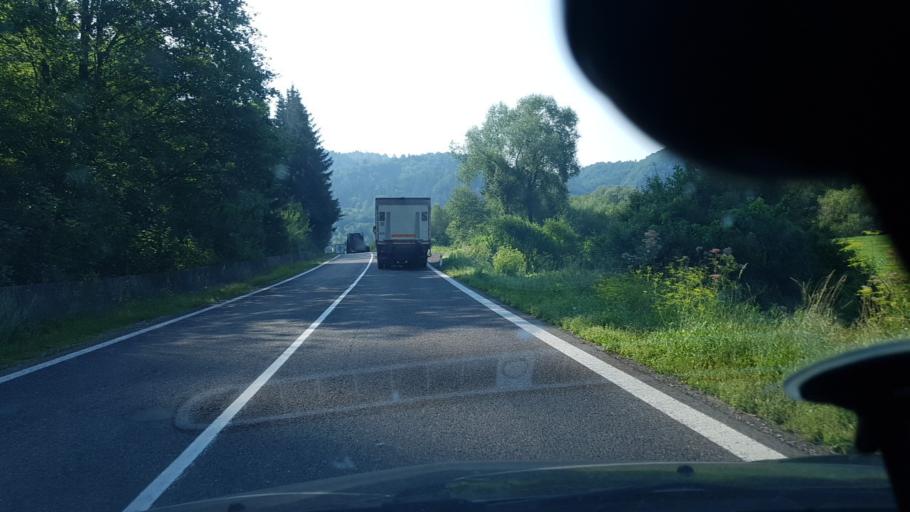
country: SK
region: Zilinsky
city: Tvrdosin
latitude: 49.2948
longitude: 19.4899
